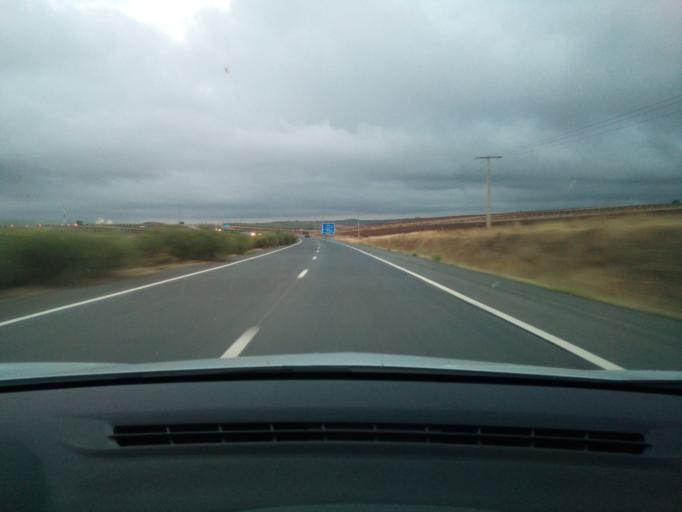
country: MA
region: Meknes-Tafilalet
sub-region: Meknes
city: Meknes
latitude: 33.8487
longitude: -5.6201
